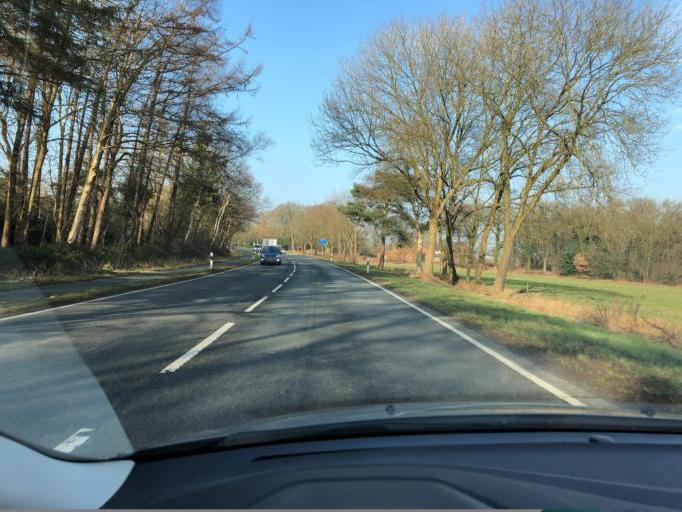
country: DE
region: Lower Saxony
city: Westerstede
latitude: 53.2899
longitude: 7.8883
